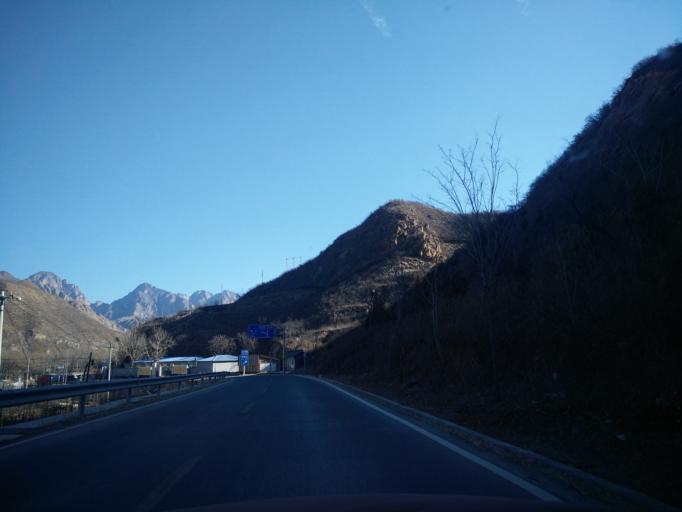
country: CN
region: Beijing
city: Zhaitang
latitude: 40.0655
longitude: 115.7141
